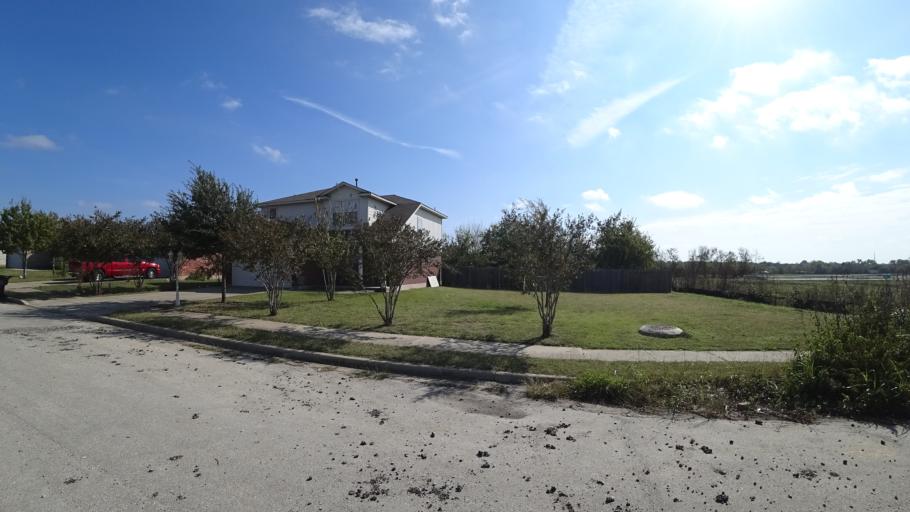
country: US
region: Texas
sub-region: Travis County
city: Pflugerville
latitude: 30.4152
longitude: -97.6369
